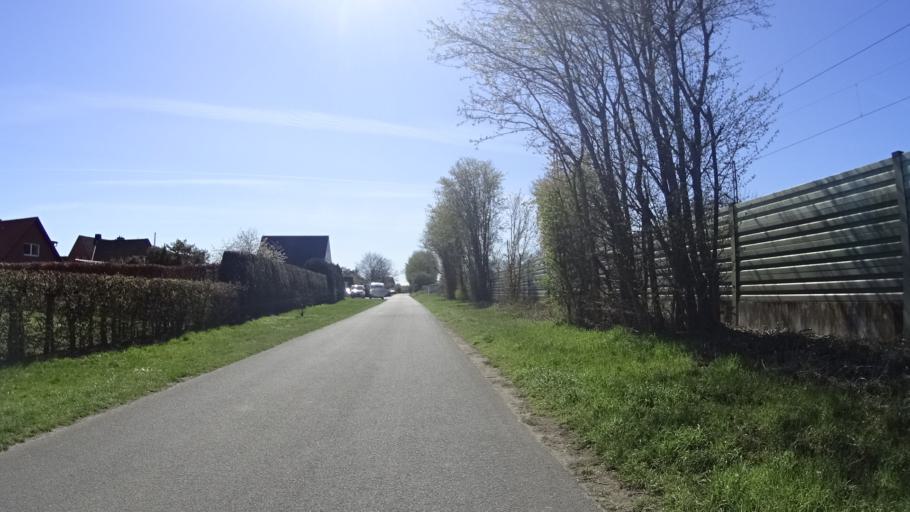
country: DE
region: North Rhine-Westphalia
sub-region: Regierungsbezirk Munster
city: Haltern
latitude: 51.7744
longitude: 7.2299
